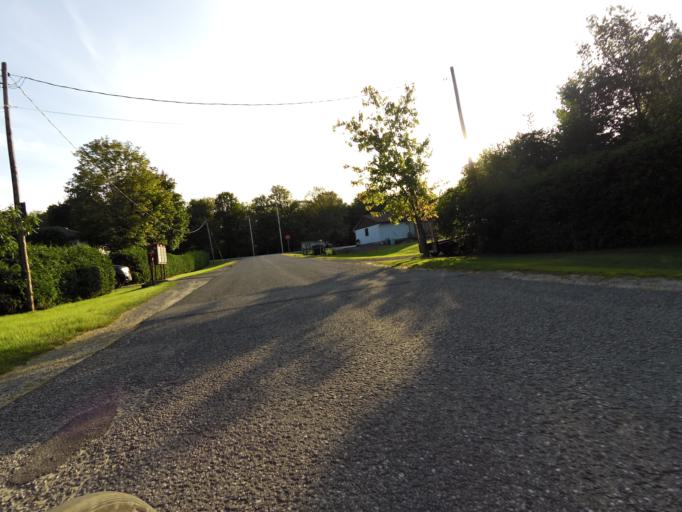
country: CA
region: Ontario
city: Bells Corners
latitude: 45.3783
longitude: -75.9614
